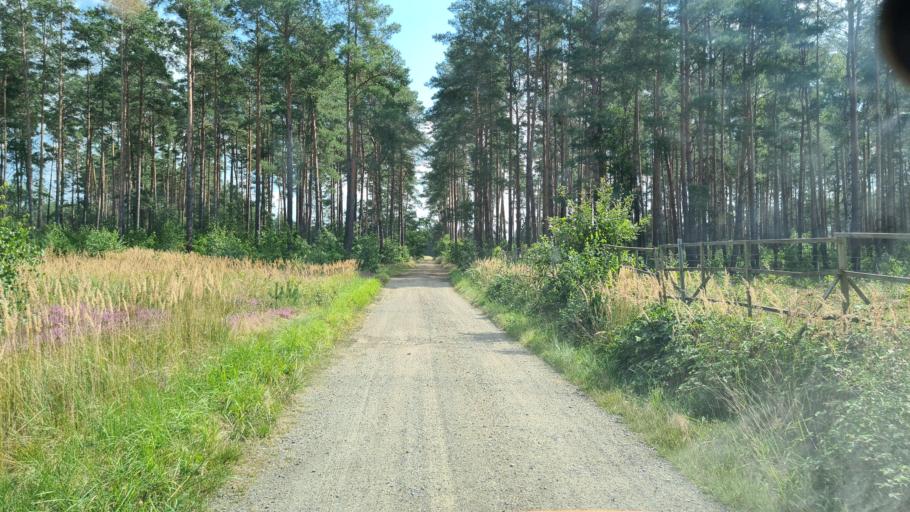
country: DE
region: Brandenburg
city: Hohenbucko
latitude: 51.7897
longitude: 13.5737
